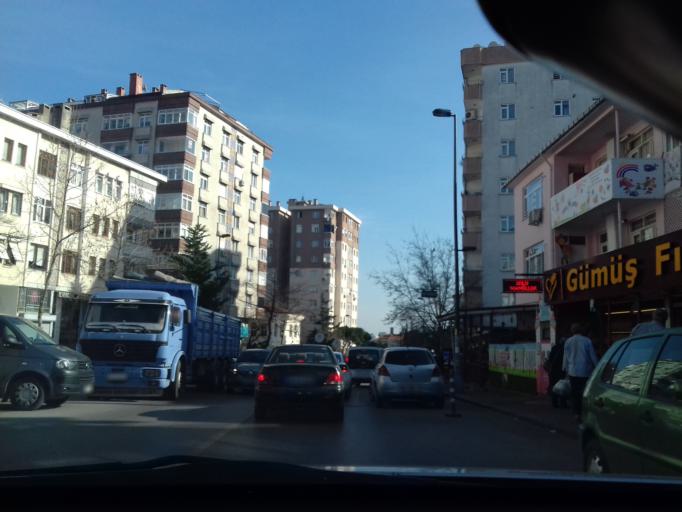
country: TR
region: Istanbul
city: Umraniye
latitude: 41.0225
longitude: 29.0808
